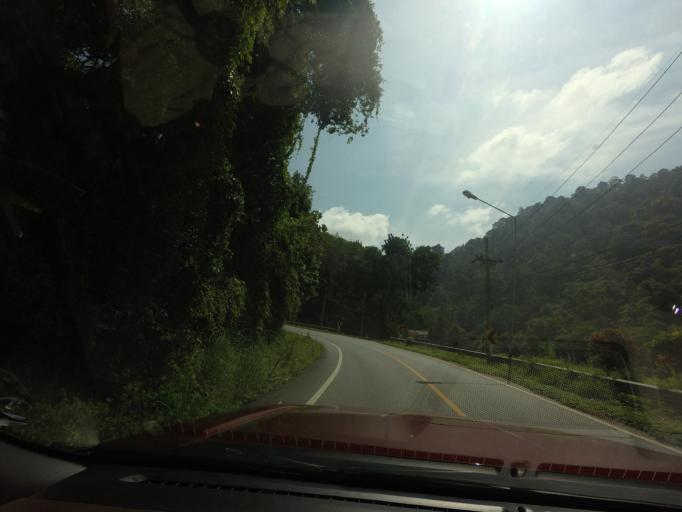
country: TH
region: Yala
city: Betong
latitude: 5.8329
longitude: 101.0795
